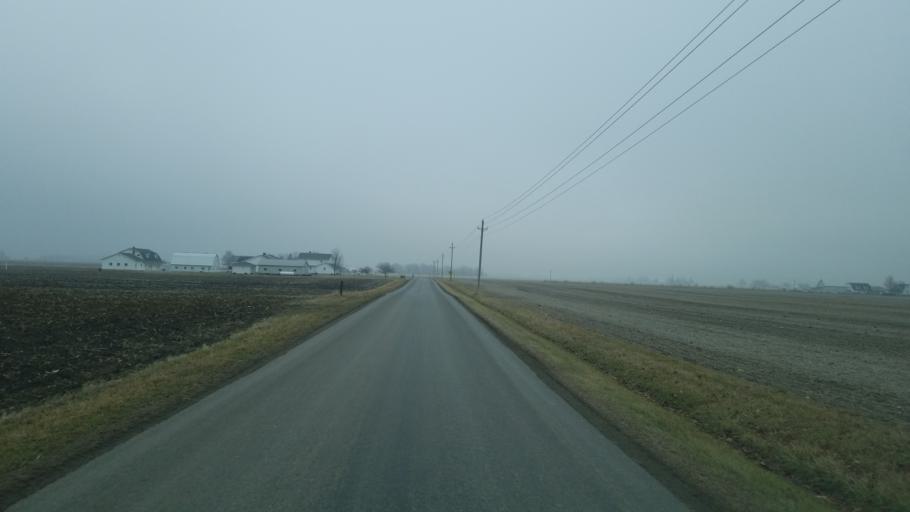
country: US
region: Indiana
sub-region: Adams County
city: Berne
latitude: 40.7000
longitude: -85.0003
